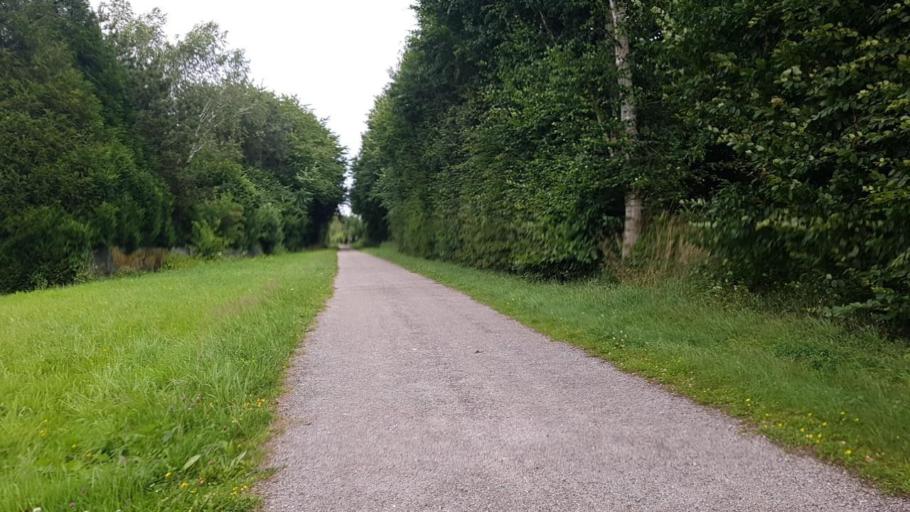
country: FR
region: Picardie
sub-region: Departement de l'Aisne
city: Origny-en-Thierache
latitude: 49.9281
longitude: 4.0318
